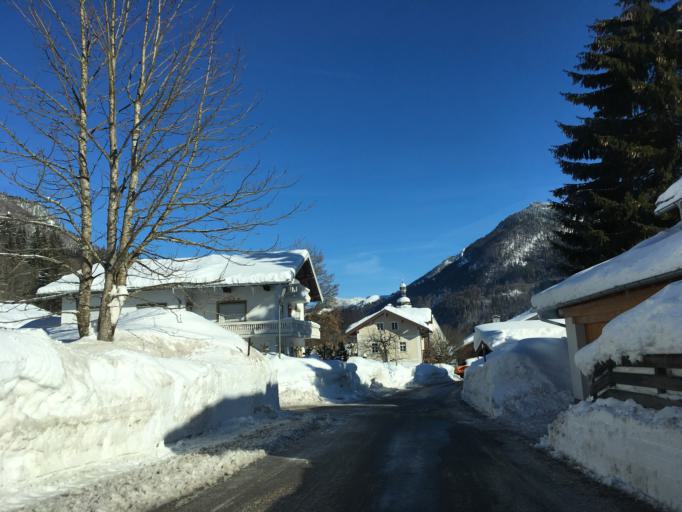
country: AT
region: Tyrol
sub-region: Politischer Bezirk Kufstein
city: Rettenschoss
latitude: 47.6901
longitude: 12.2604
